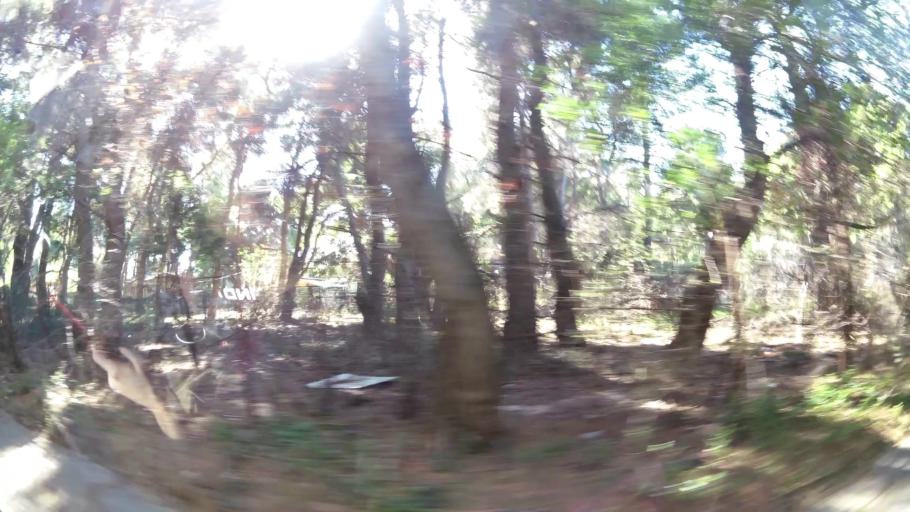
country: GR
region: Attica
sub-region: Nomarchia Athinas
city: Ekali
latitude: 38.1063
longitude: 23.8289
